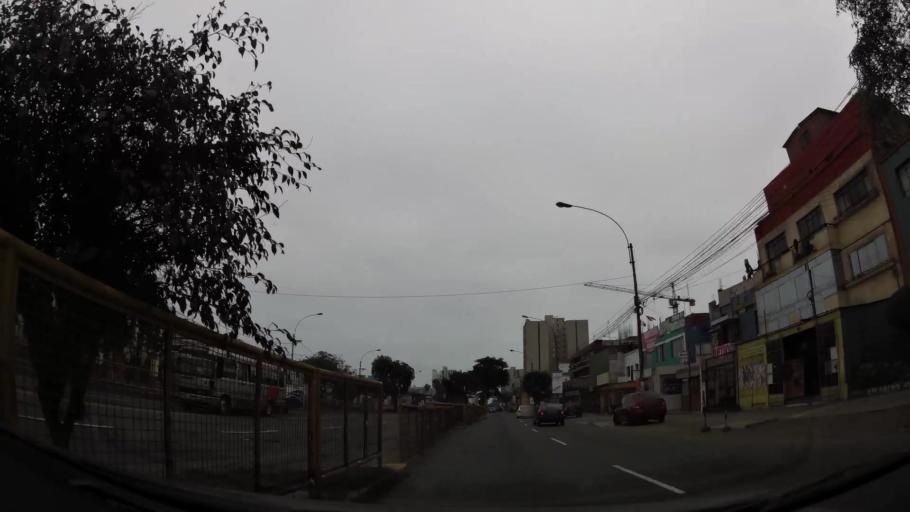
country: PE
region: Lima
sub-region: Lima
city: San Isidro
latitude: -12.0837
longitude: -77.0610
